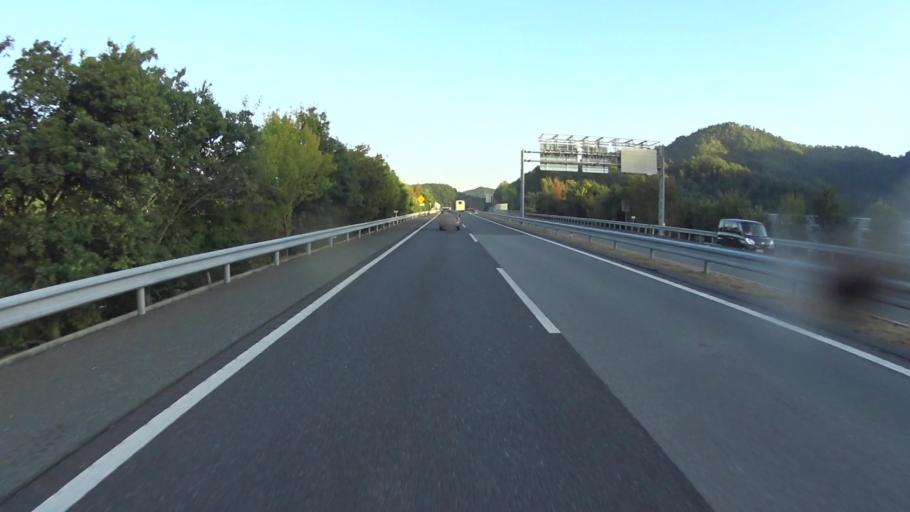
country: JP
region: Kyoto
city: Kameoka
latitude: 35.0839
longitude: 135.5080
